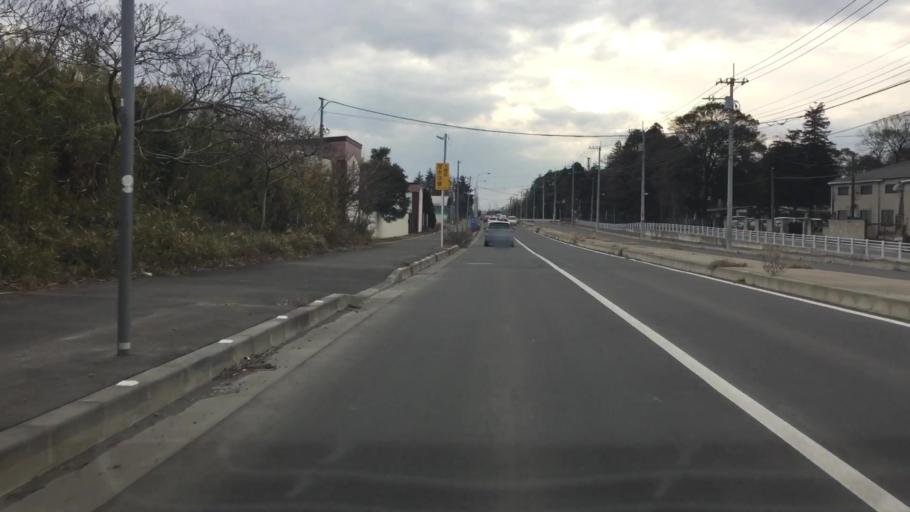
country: JP
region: Chiba
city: Shiroi
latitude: 35.8003
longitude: 140.0963
